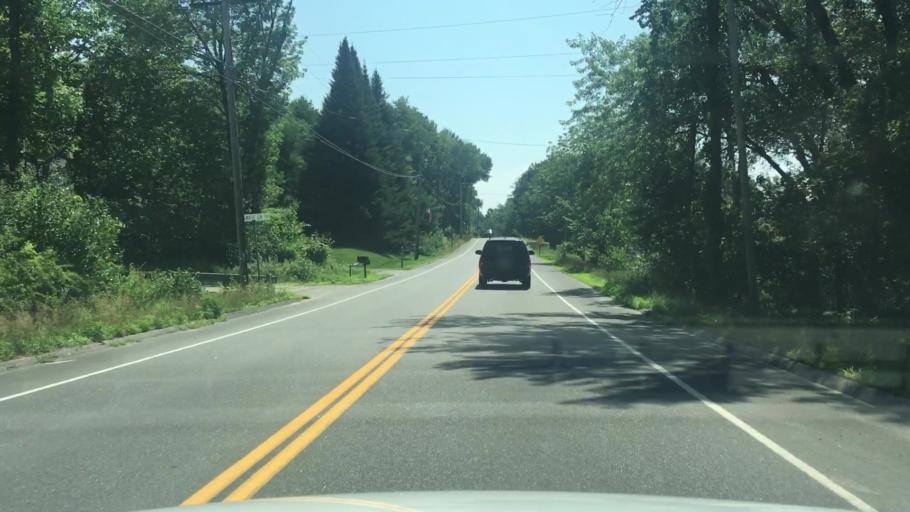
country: US
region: Maine
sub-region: Cumberland County
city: Cumberland Center
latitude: 43.8039
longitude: -70.2733
